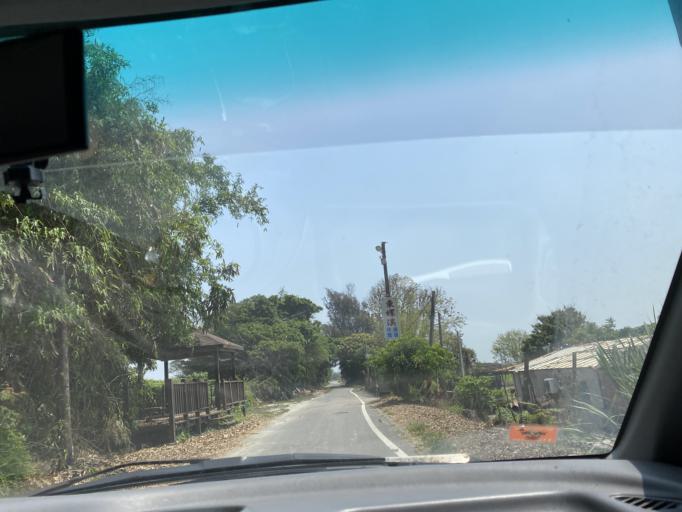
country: TW
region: Taiwan
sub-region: Changhua
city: Chang-hua
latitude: 23.9954
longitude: 120.4126
